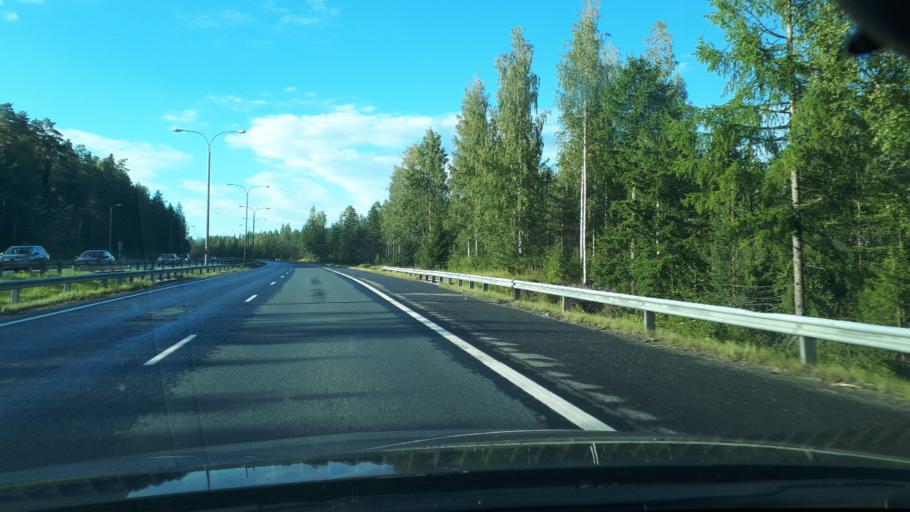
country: FI
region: Northern Savo
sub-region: Kuopio
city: Siilinjaervi
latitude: 63.0622
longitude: 27.6708
